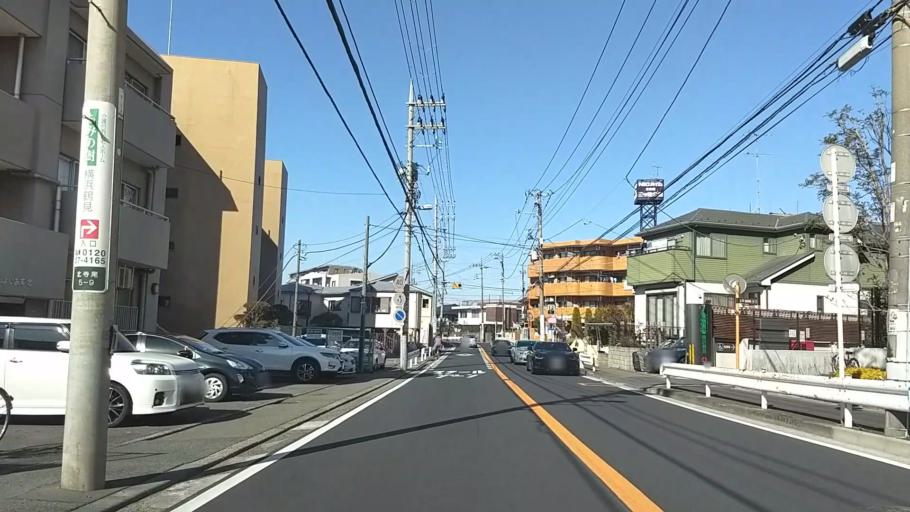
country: JP
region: Kanagawa
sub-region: Kawasaki-shi
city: Kawasaki
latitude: 35.5137
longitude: 139.6574
